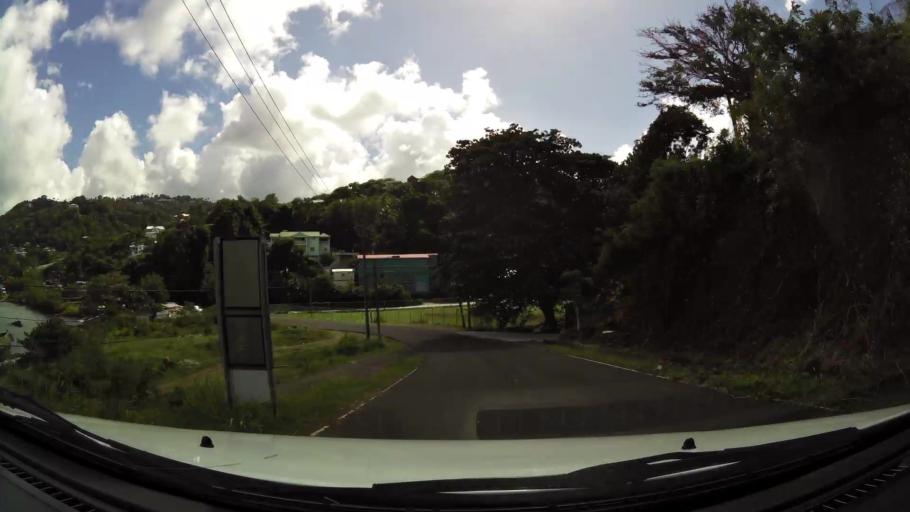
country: LC
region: Castries Quarter
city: Castries
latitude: 14.0128
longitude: -61.0026
